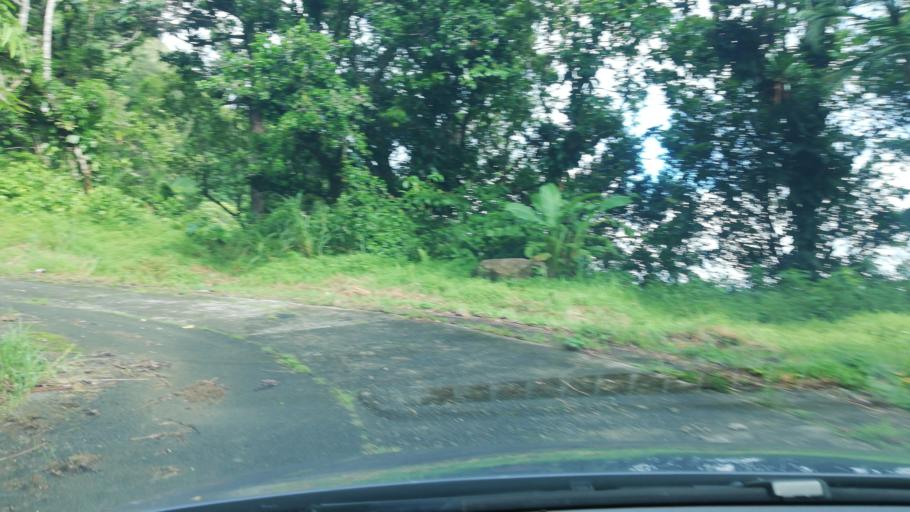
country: GP
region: Guadeloupe
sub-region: Guadeloupe
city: Bouillante
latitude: 16.1850
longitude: -61.7466
